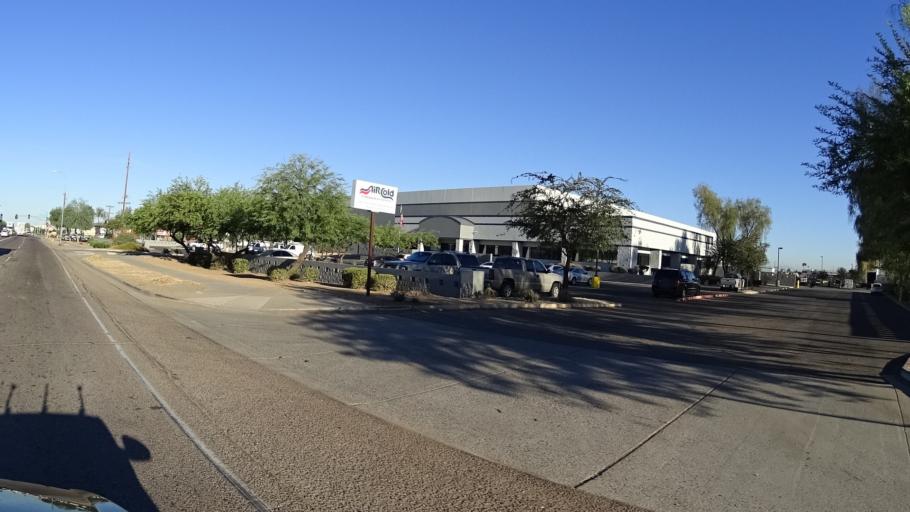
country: US
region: Arizona
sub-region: Maricopa County
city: Tolleson
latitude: 33.4372
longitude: -112.2020
